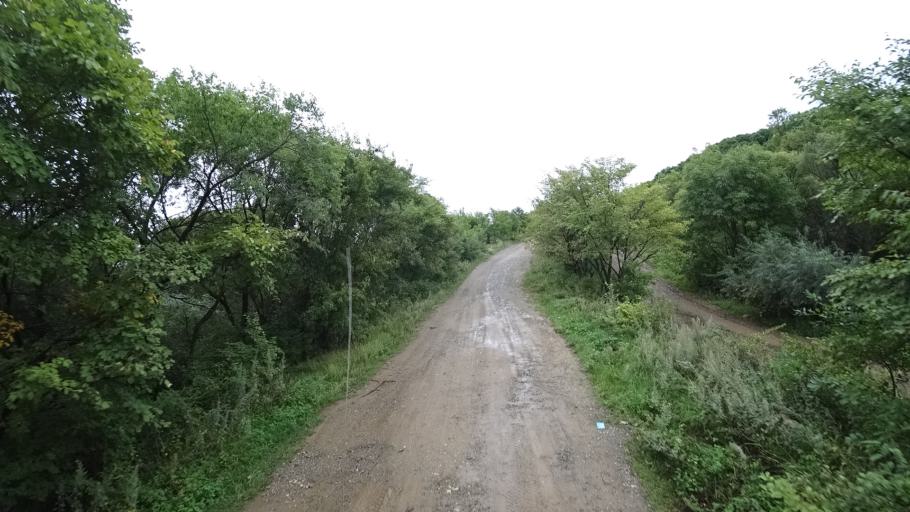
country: RU
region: Primorskiy
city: Monastyrishche
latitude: 44.2756
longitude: 132.4051
